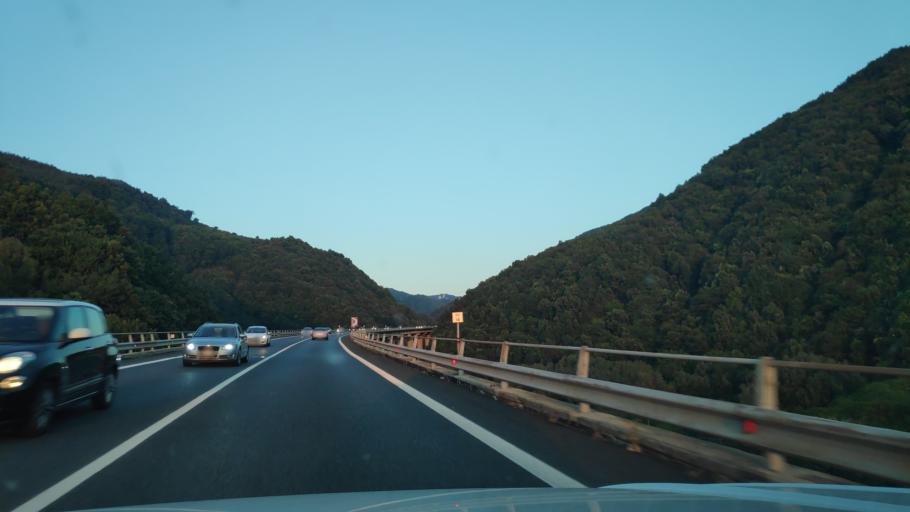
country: IT
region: Calabria
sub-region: Provincia di Reggio Calabria
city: Anoia Superiore
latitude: 38.4174
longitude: 16.1223
